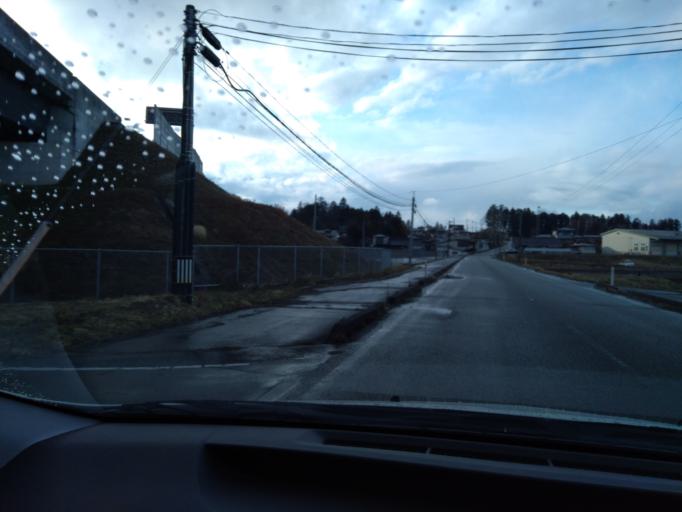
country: JP
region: Iwate
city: Ichinoseki
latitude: 38.7369
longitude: 141.1237
